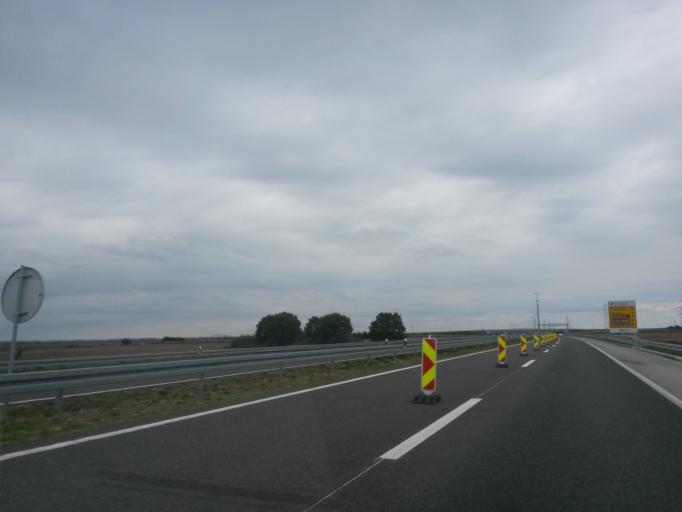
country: HR
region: Osjecko-Baranjska
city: Josipovac
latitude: 45.5689
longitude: 18.5498
